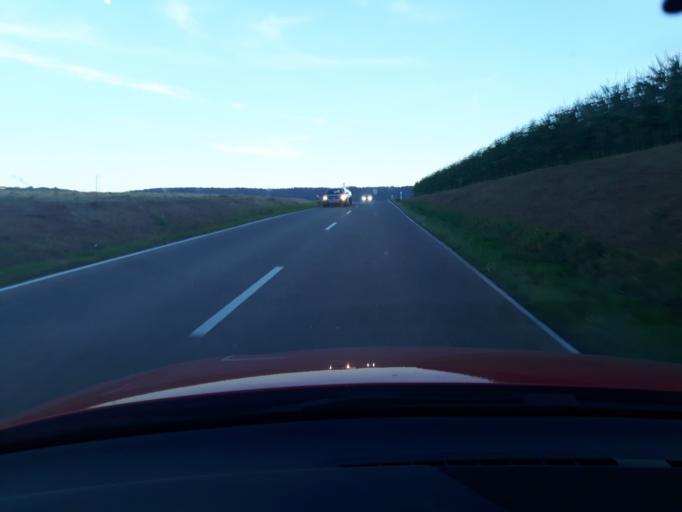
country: DE
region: Baden-Wuerttemberg
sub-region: Regierungsbezirk Stuttgart
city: Cleebronn
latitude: 49.0602
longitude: 9.0291
